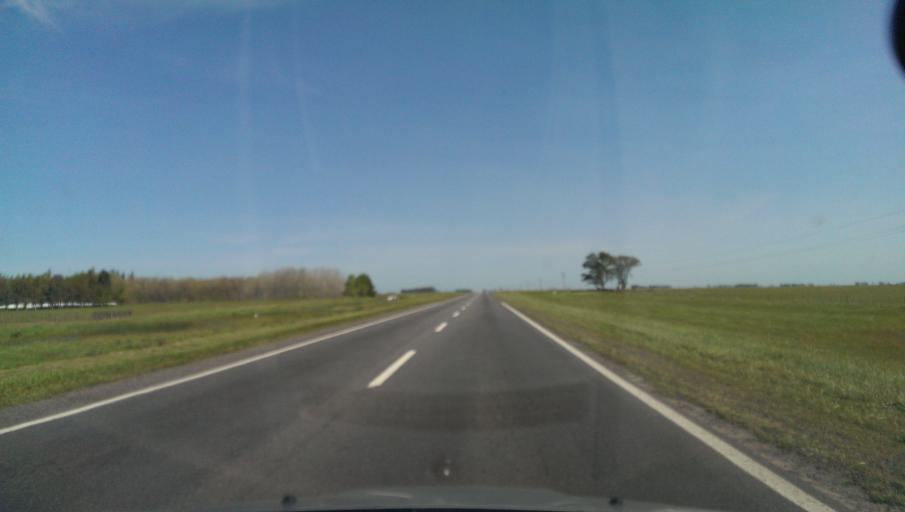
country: AR
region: Buenos Aires
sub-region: Partido de Azul
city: Azul
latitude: -36.5663
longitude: -59.6398
